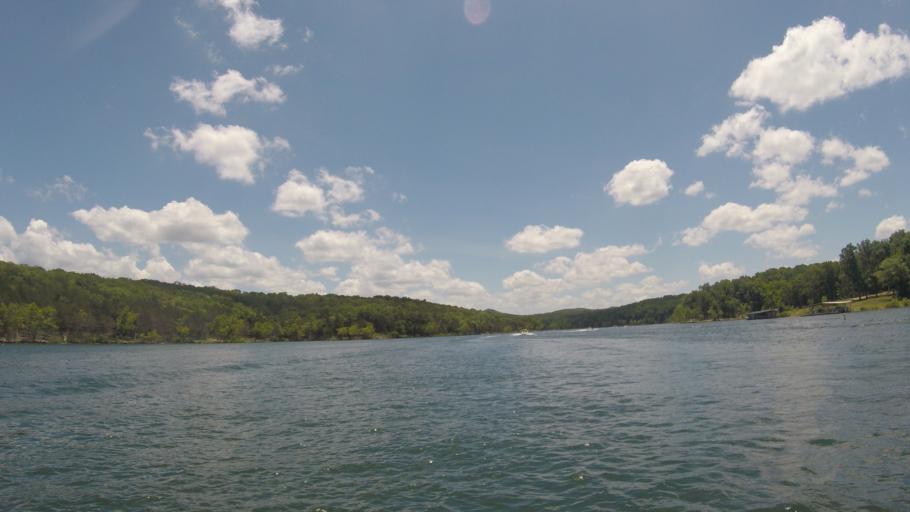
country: US
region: Missouri
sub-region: Barry County
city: Shell Knob
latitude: 36.5804
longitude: -93.5667
